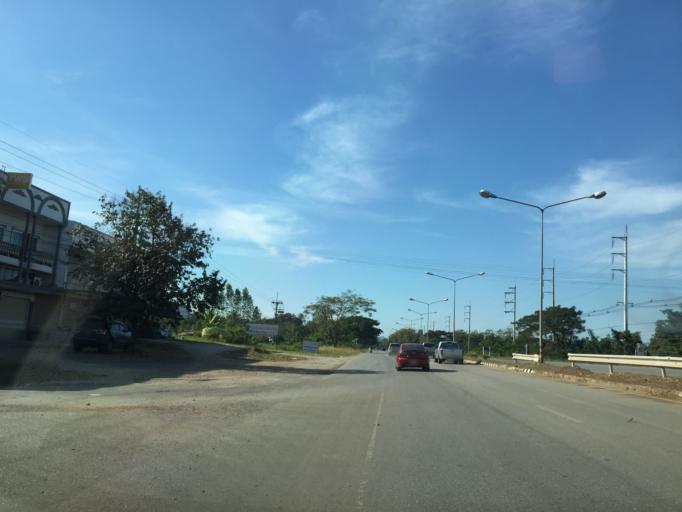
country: TH
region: Loei
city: Wang Saphung
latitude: 17.3163
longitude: 101.7693
